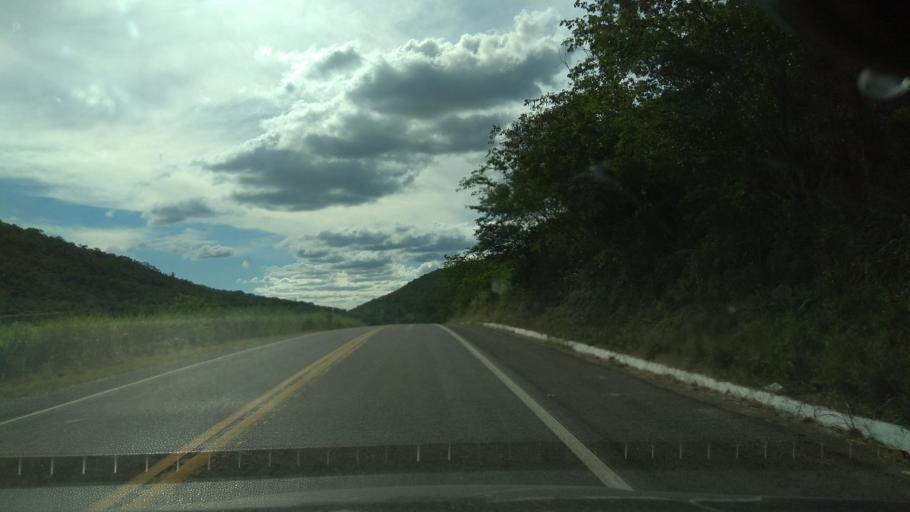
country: BR
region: Bahia
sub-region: Jequie
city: Jequie
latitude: -13.8959
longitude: -40.0207
